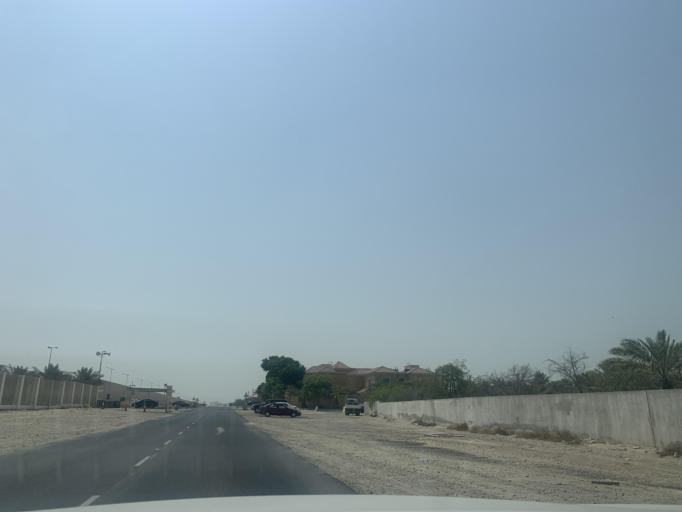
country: BH
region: Central Governorate
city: Madinat Hamad
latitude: 26.1529
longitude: 50.4723
